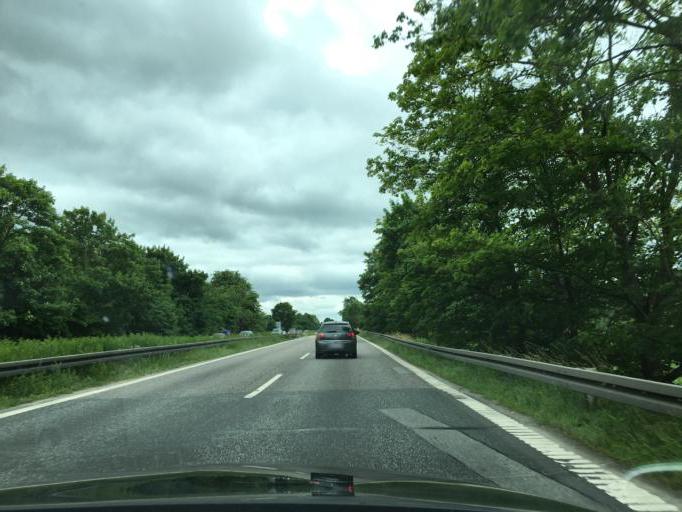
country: DK
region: Capital Region
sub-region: Fredensborg Kommune
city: Kokkedal
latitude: 55.9003
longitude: 12.4738
